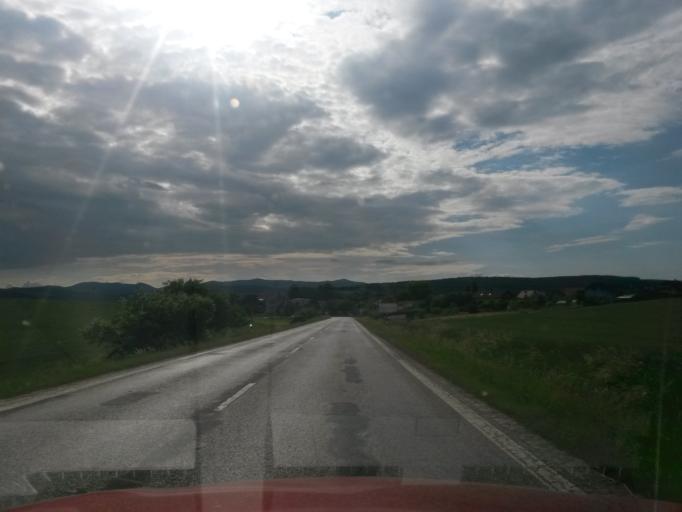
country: SK
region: Presovsky
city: Sabinov
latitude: 49.0091
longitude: 21.1331
